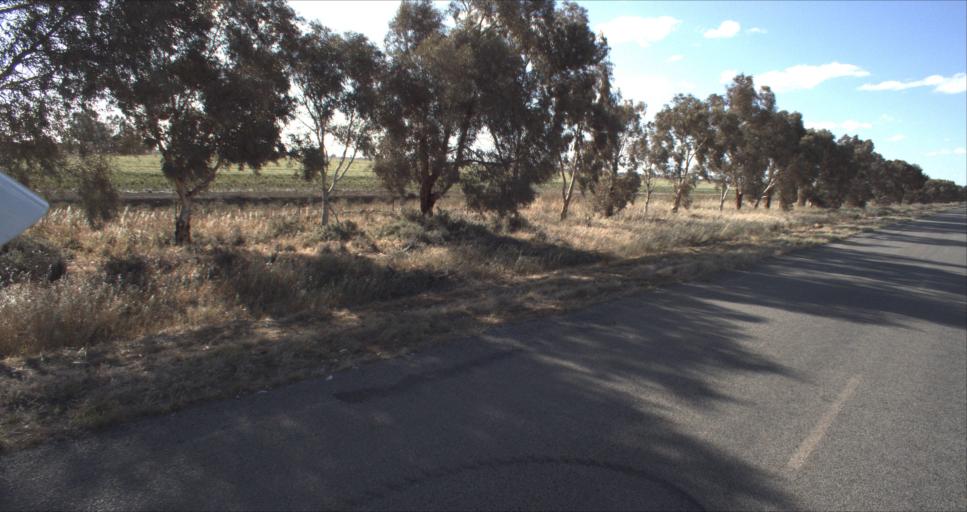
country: AU
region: New South Wales
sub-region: Leeton
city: Leeton
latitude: -34.5487
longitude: 146.2793
